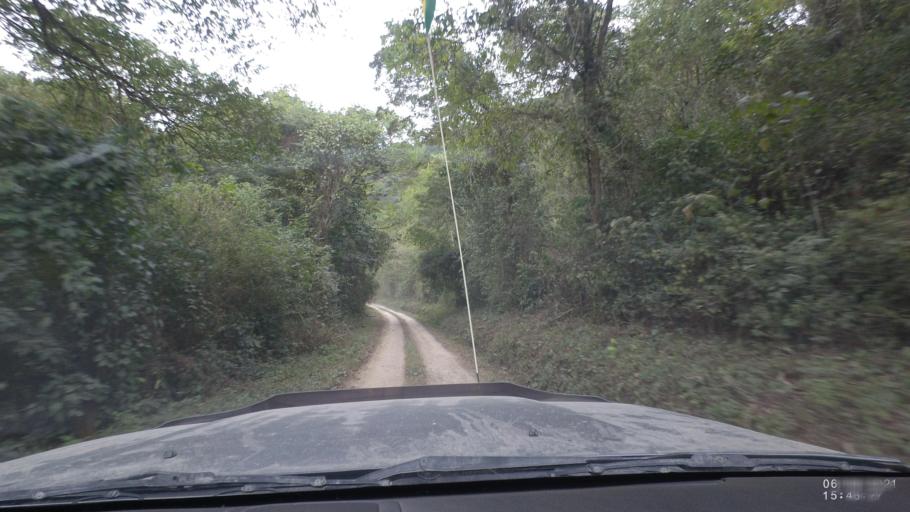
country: BO
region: La Paz
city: Quime
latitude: -16.5948
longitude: -66.7088
